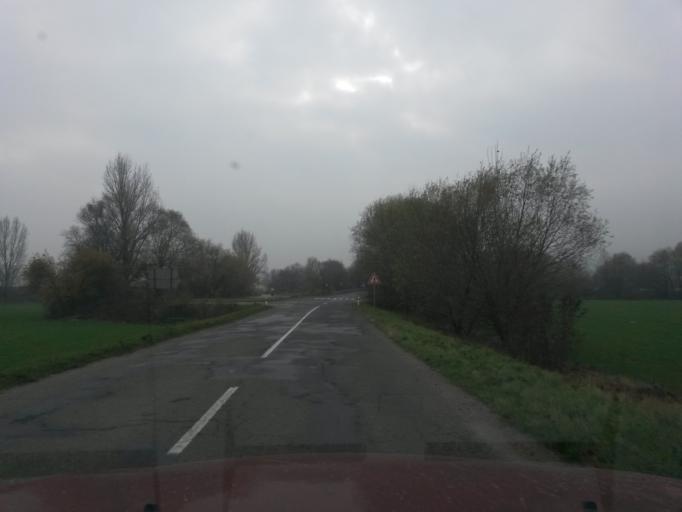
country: SK
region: Presovsky
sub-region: Okres Presov
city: Presov
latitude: 48.8604
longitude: 21.2708
